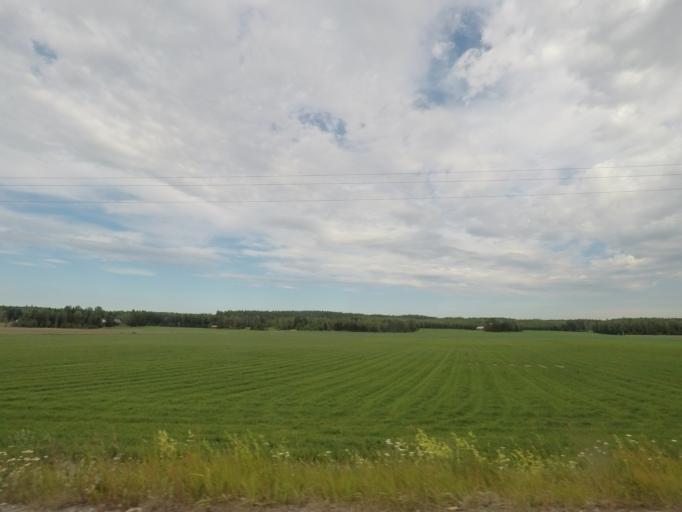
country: FI
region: Paijanne Tavastia
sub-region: Lahti
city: Hollola
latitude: 60.8555
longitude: 25.4989
